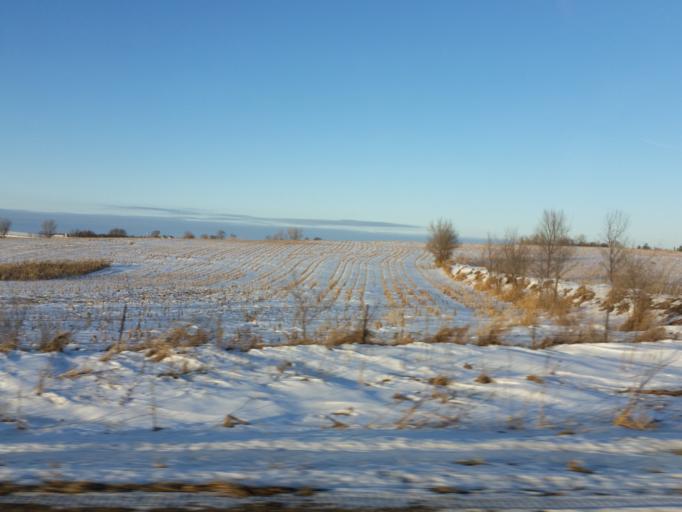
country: US
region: Iowa
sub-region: Butler County
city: Allison
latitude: 42.7449
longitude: -92.8951
